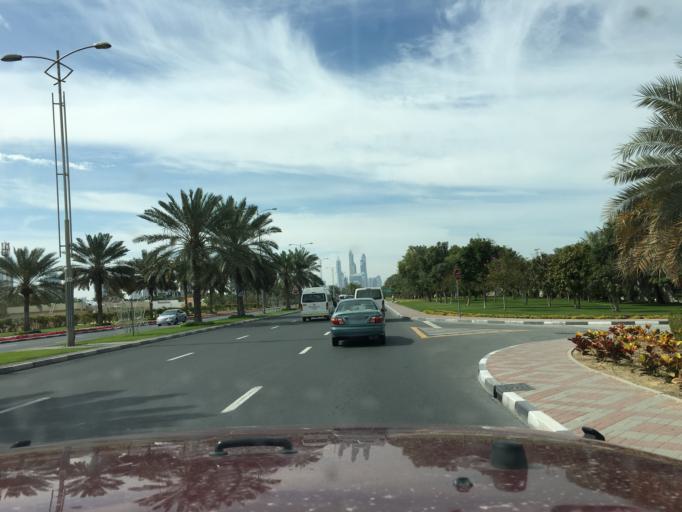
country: AE
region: Dubai
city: Dubai
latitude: 25.1256
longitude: 55.1815
